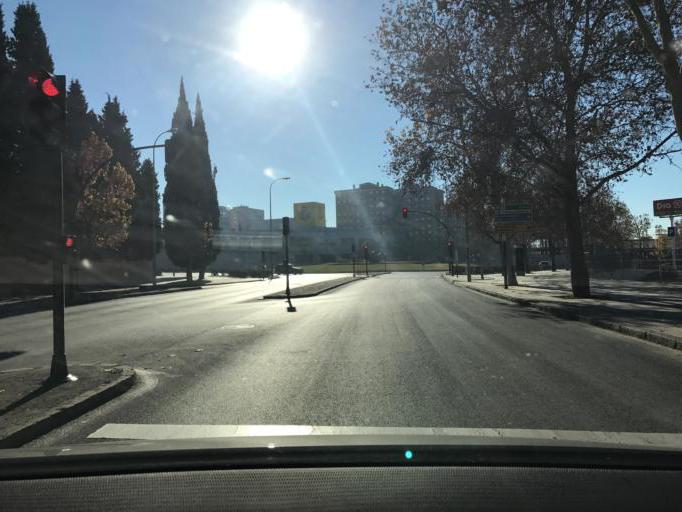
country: ES
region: Andalusia
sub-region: Provincia de Granada
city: Granada
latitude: 37.1998
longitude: -3.6049
